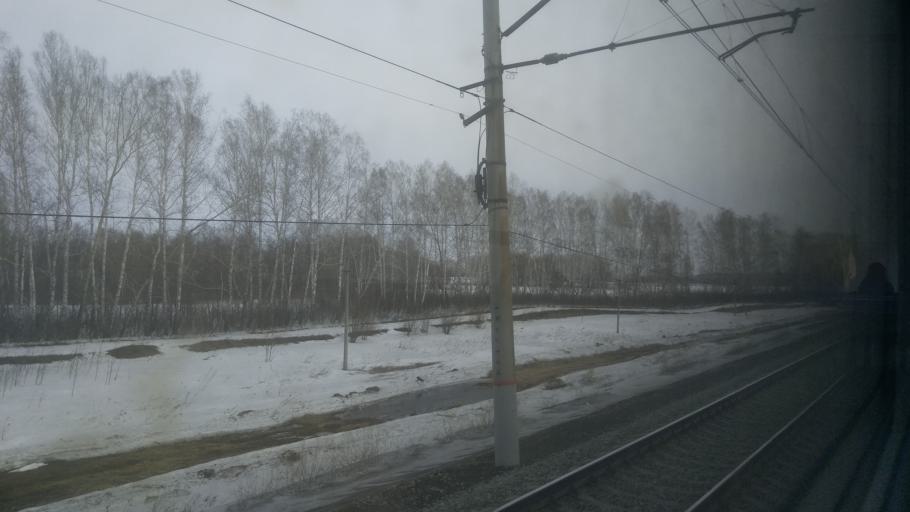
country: RU
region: Novosibirsk
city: Bolotnoye
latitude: 55.7082
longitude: 84.6084
